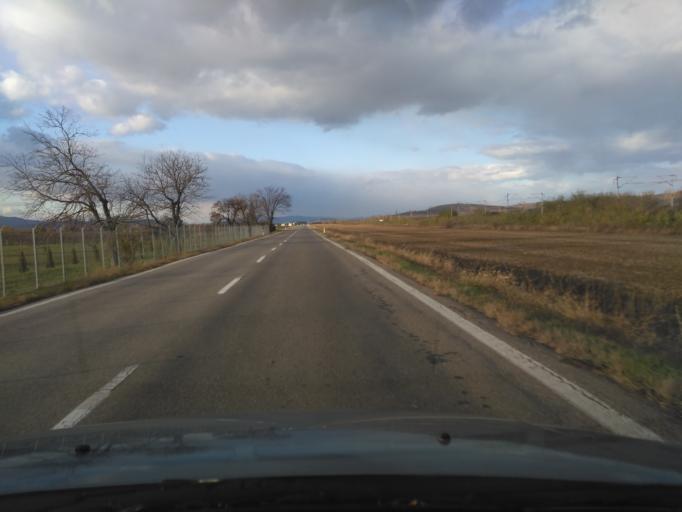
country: HU
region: Borsod-Abauj-Zemplen
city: Satoraljaujhely
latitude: 48.4165
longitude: 21.6642
